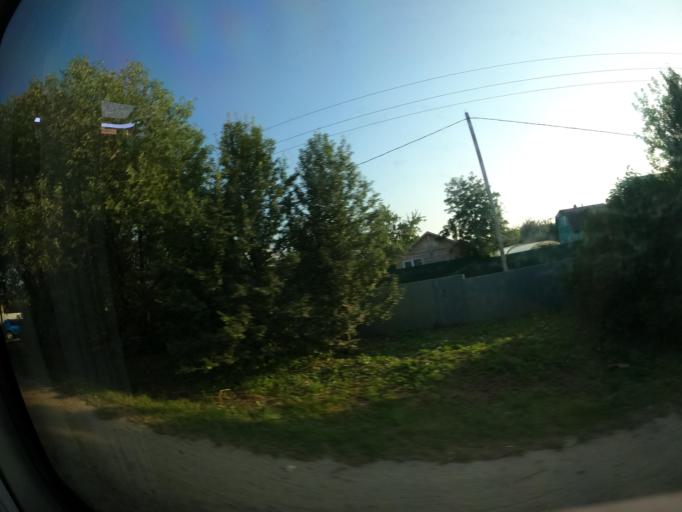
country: RU
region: Moskovskaya
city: Serpukhov
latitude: 54.9403
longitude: 37.3543
